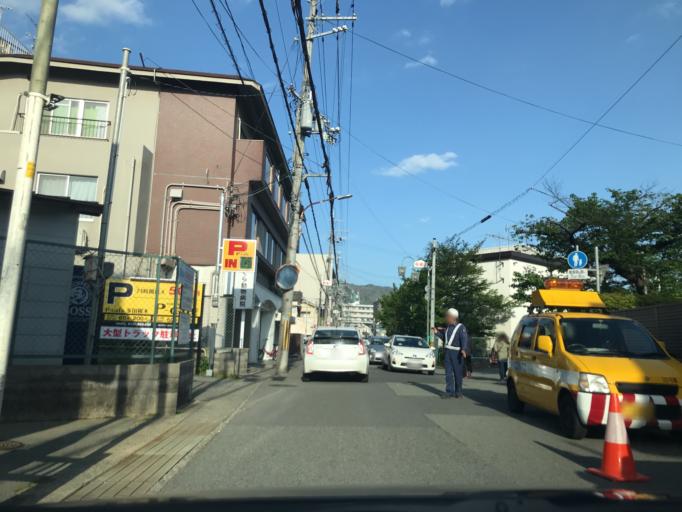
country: JP
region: Osaka
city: Ikeda
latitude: 34.8610
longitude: 135.4140
